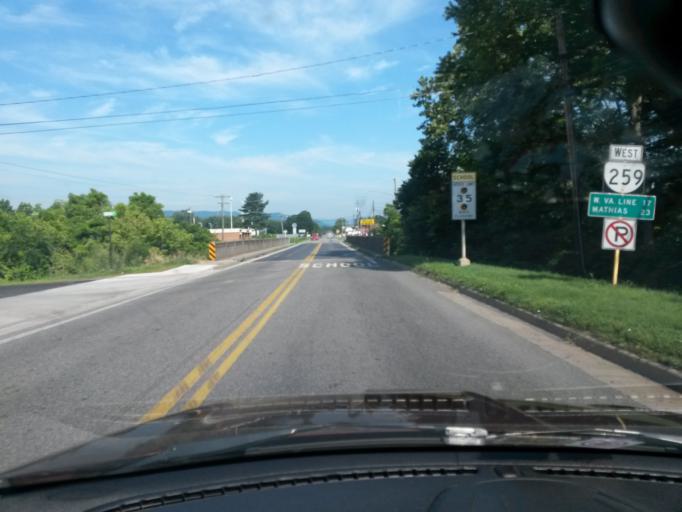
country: US
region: Virginia
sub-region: Rockingham County
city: Broadway
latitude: 38.6179
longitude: -78.7975
